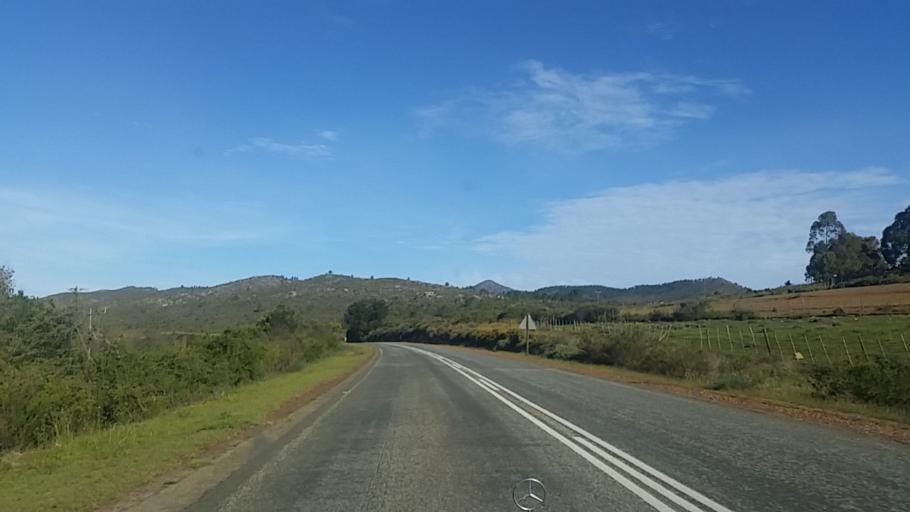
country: ZA
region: Western Cape
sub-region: Eden District Municipality
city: Knysna
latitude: -33.7732
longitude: 22.9014
